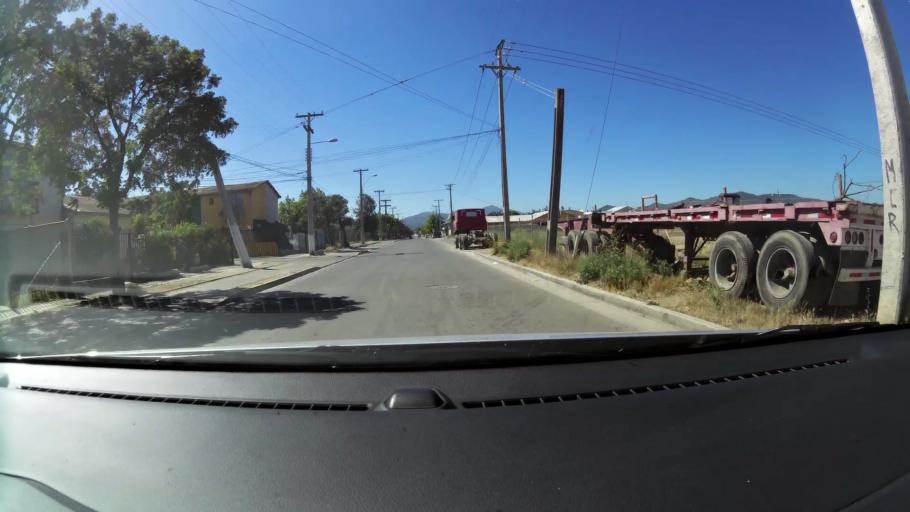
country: CL
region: Valparaiso
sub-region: Provincia de Marga Marga
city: Quilpue
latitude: -33.3062
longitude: -71.4142
